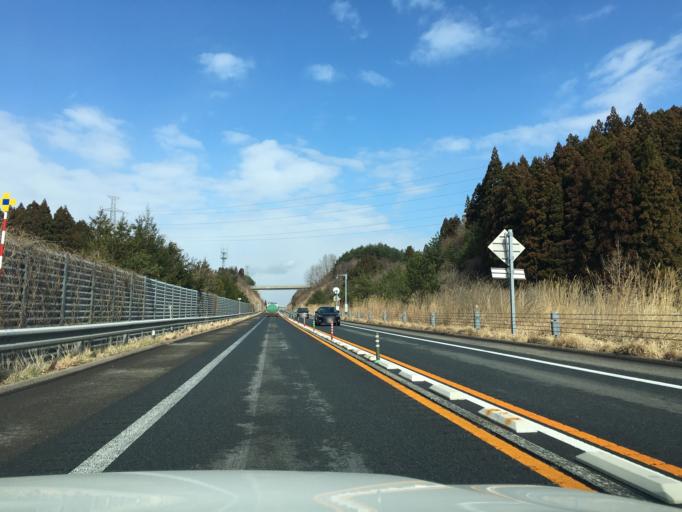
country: JP
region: Akita
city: Akita Shi
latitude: 39.8058
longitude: 140.0955
